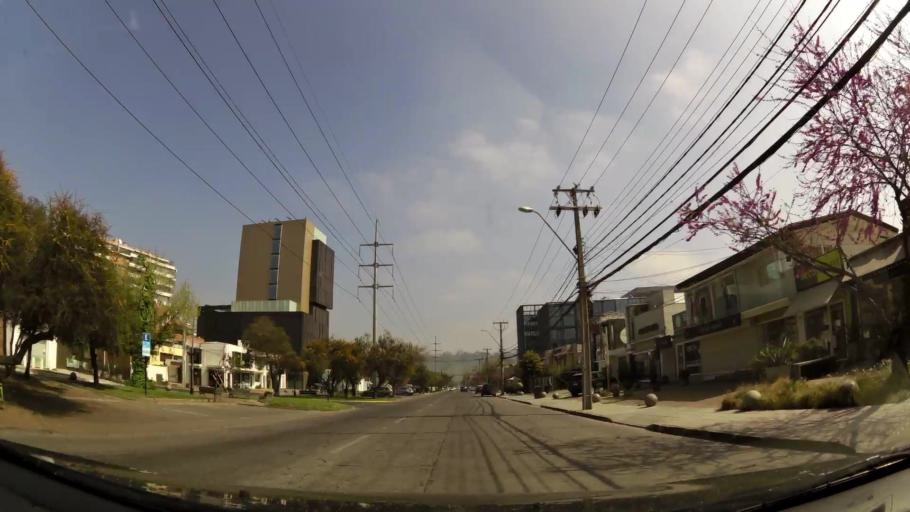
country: CL
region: Santiago Metropolitan
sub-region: Provincia de Santiago
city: Villa Presidente Frei, Nunoa, Santiago, Chile
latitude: -33.4026
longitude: -70.5916
